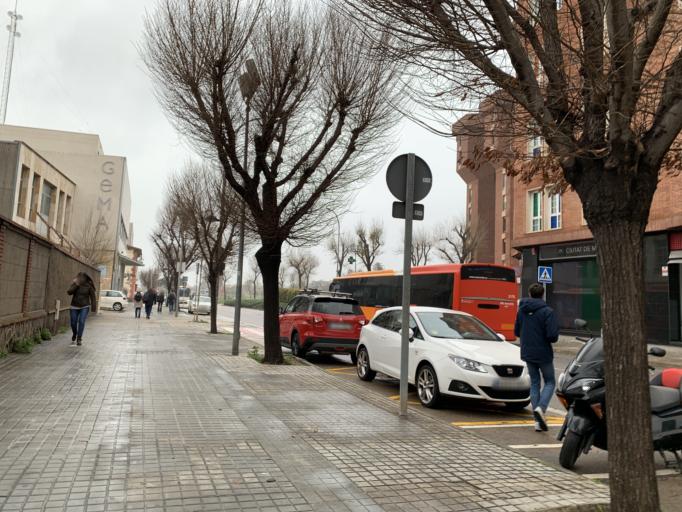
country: ES
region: Catalonia
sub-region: Provincia de Barcelona
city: Mataro
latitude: 41.5316
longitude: 2.4373
